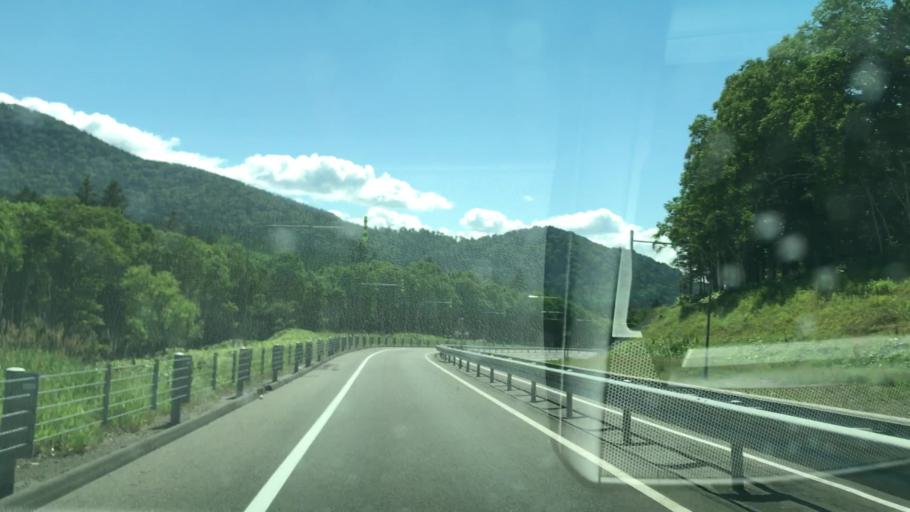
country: JP
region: Hokkaido
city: Otofuke
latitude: 42.9787
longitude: 142.7274
